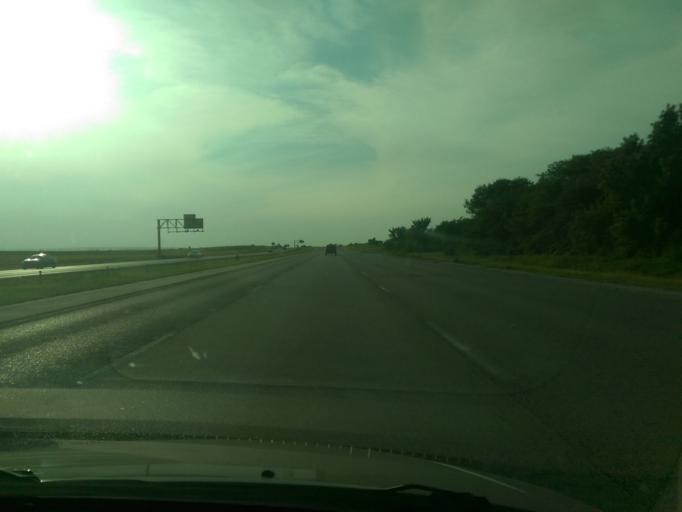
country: US
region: Missouri
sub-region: Platte County
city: Platte City
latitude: 39.3292
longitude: -94.7118
